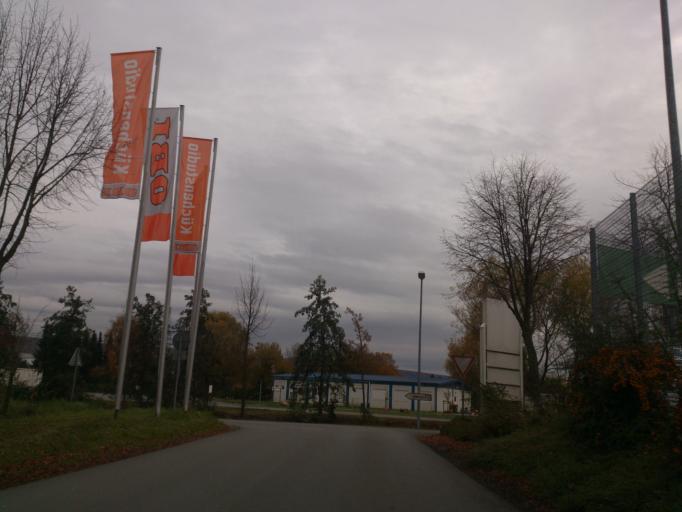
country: DE
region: North Rhine-Westphalia
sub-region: Regierungsbezirk Detmold
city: Hoexter
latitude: 51.7867
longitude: 9.3931
